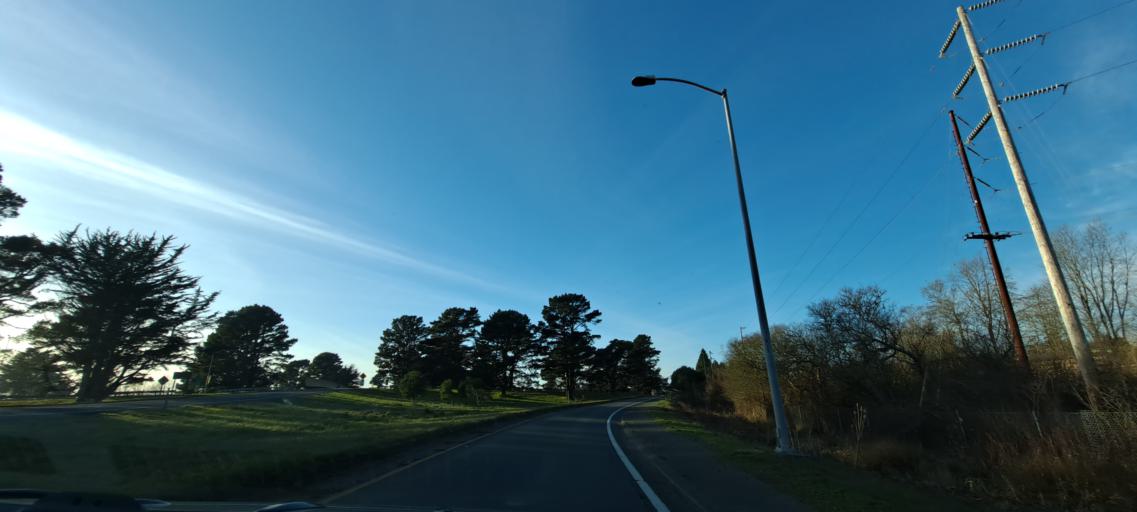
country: US
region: California
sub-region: Humboldt County
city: Arcata
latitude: 40.8623
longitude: -124.0802
